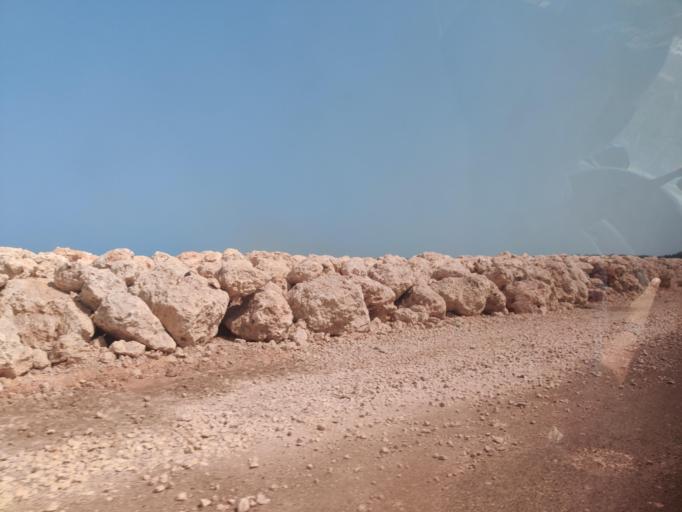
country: CO
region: Bolivar
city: Turbana
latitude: 10.1891
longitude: -75.6381
